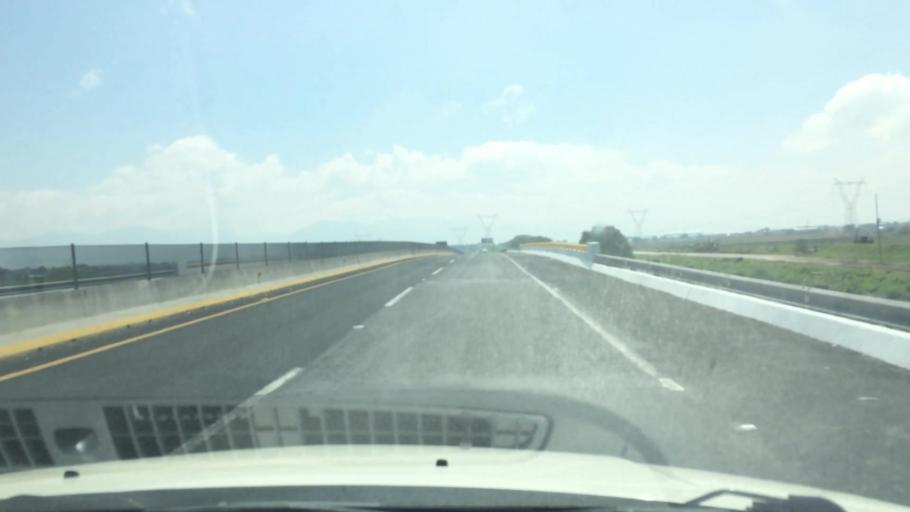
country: MX
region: Mexico
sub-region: Otzolotepec
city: La Y
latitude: 19.4050
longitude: -99.5939
